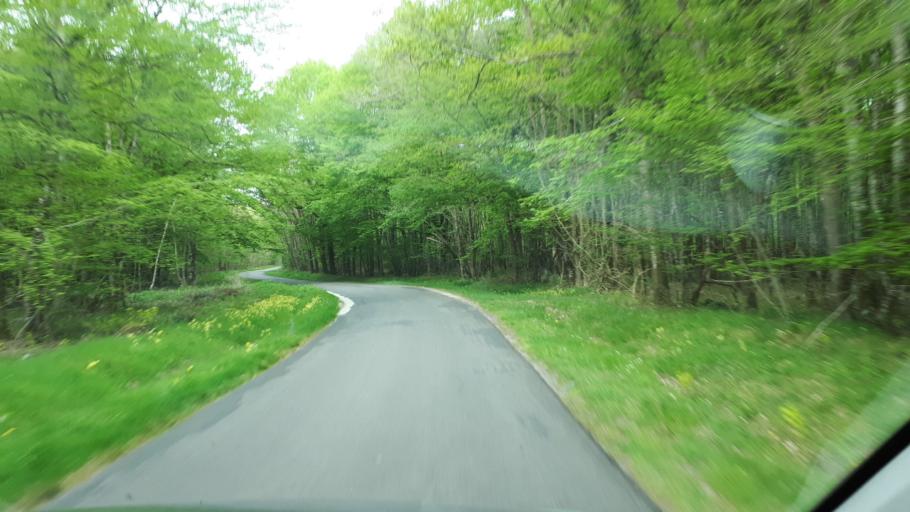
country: FR
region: Centre
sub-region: Departement du Loir-et-Cher
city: Contres
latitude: 47.3625
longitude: 1.4344
